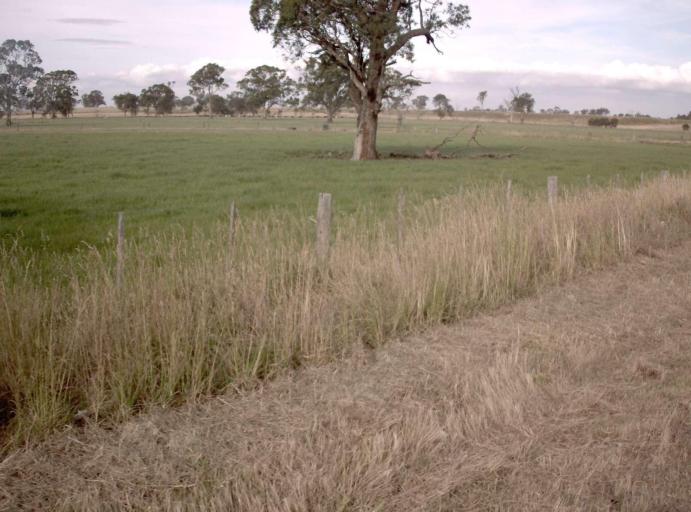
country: AU
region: Victoria
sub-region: Wellington
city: Heyfield
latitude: -37.9830
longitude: 146.8204
